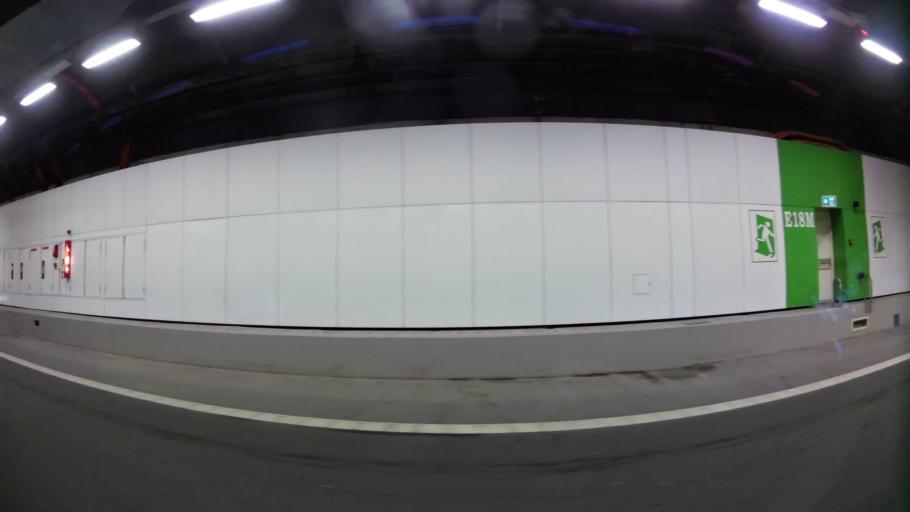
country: SG
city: Singapore
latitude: 1.2822
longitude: 103.8673
